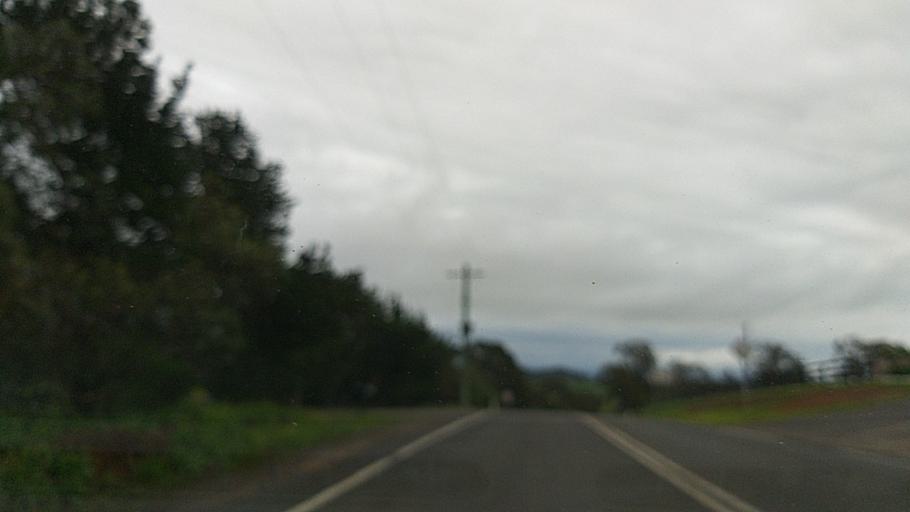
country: AU
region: New South Wales
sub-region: Wollondilly
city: Douglas Park
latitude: -34.1478
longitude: 150.7210
